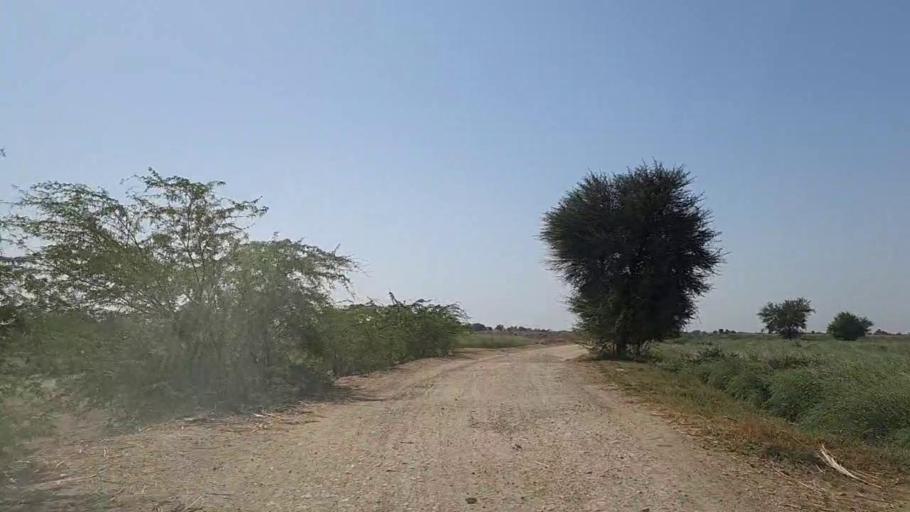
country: PK
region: Sindh
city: Samaro
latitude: 25.2271
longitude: 69.4064
